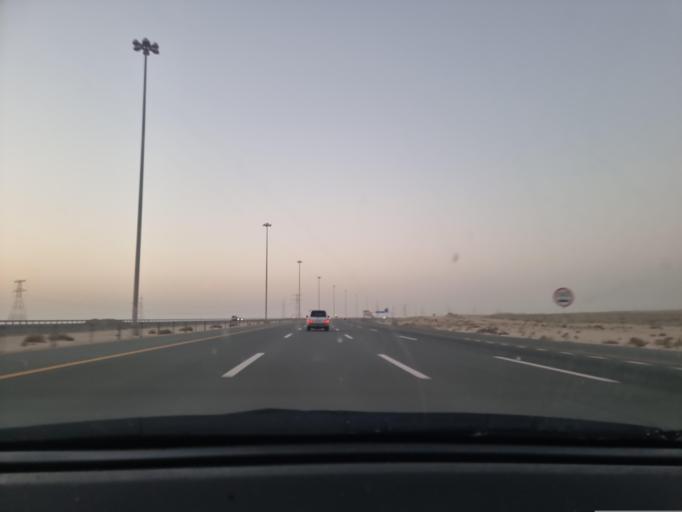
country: AE
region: Abu Dhabi
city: Abu Dhabi
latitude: 24.4466
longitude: 54.7546
